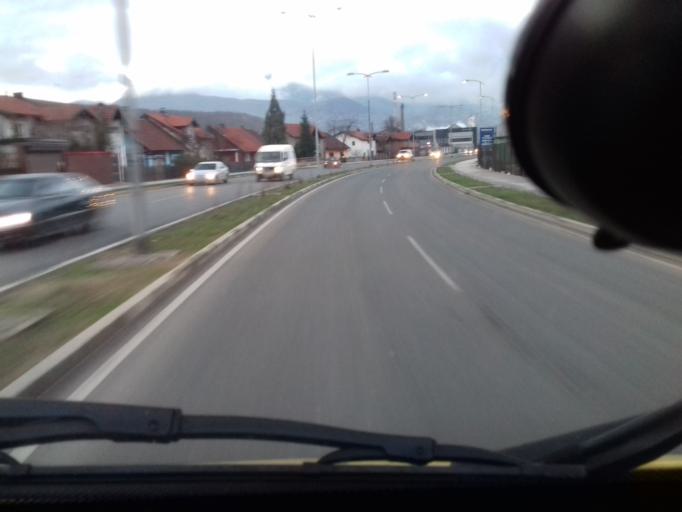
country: BA
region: Federation of Bosnia and Herzegovina
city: Zenica
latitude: 44.2052
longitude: 17.9027
